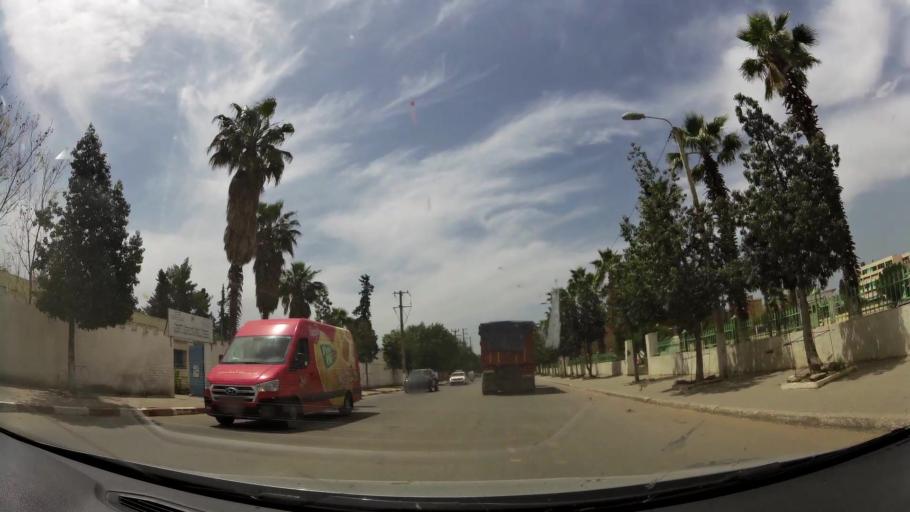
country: MA
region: Rabat-Sale-Zemmour-Zaer
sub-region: Khemisset
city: Khemisset
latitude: 33.8196
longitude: -6.0691
